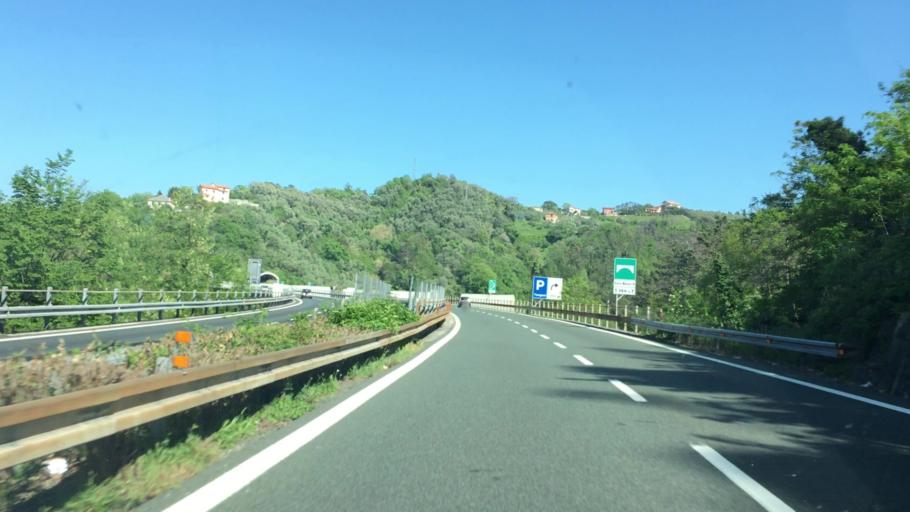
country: IT
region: Liguria
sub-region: Provincia di Genova
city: Casarza Ligure
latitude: 44.2682
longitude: 9.4462
